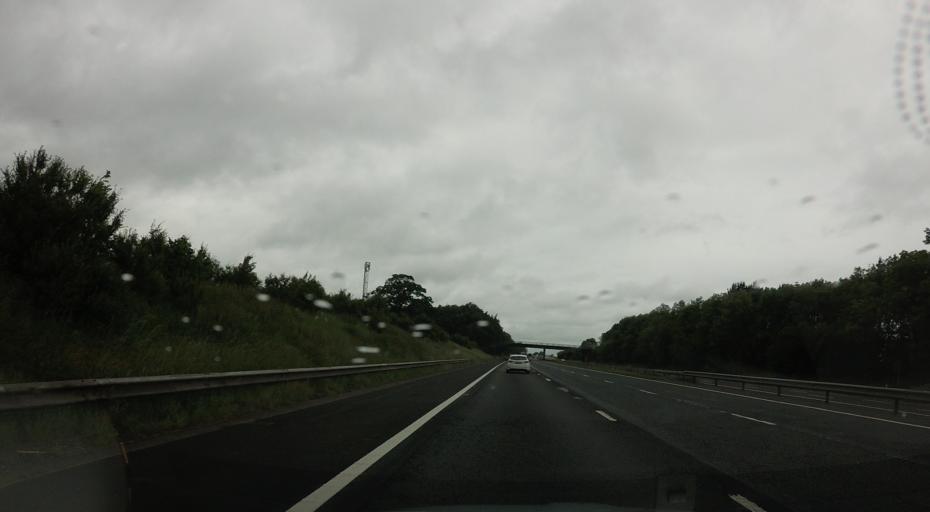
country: GB
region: England
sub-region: Cumbria
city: Penrith
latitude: 54.7208
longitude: -2.7998
